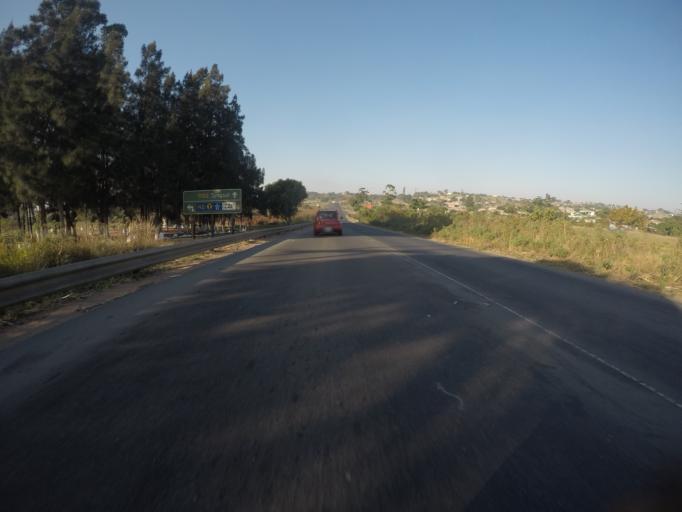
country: ZA
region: KwaZulu-Natal
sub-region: iLembe District Municipality
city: Stanger
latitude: -29.3956
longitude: 31.2517
